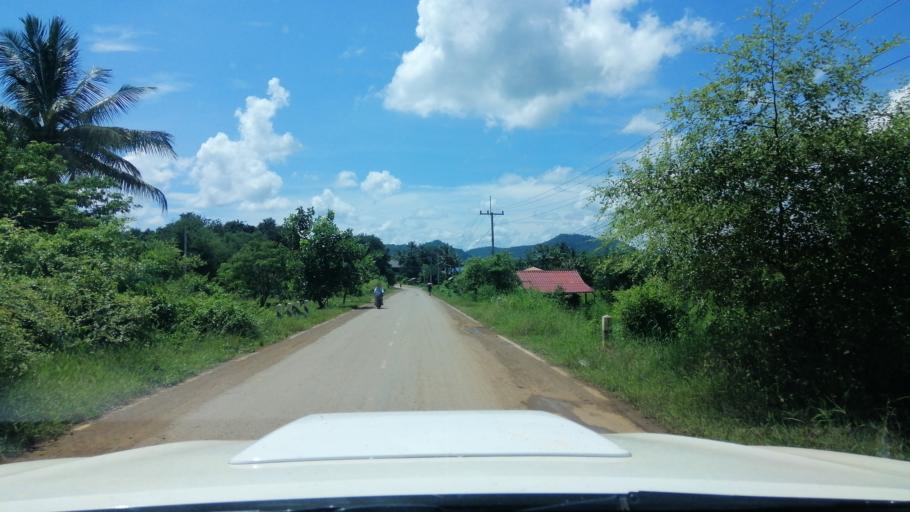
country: TH
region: Uttaradit
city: Ban Khok
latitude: 18.1356
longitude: 101.2740
